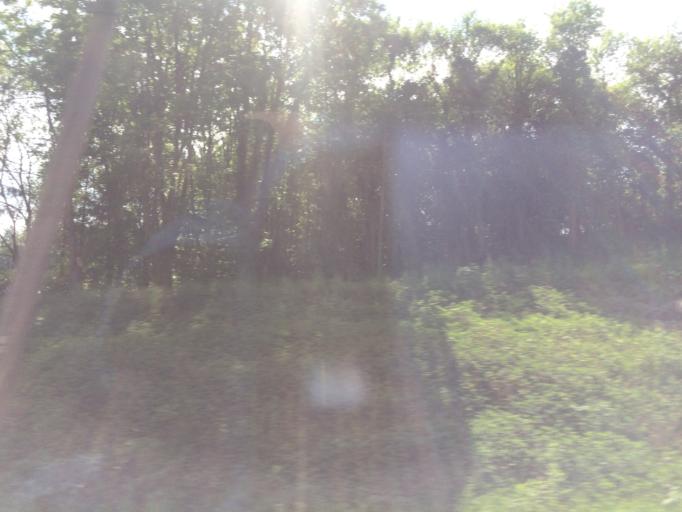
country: DE
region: Bavaria
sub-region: Regierungsbezirk Unterfranken
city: Biebelried
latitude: 49.7958
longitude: 10.0816
